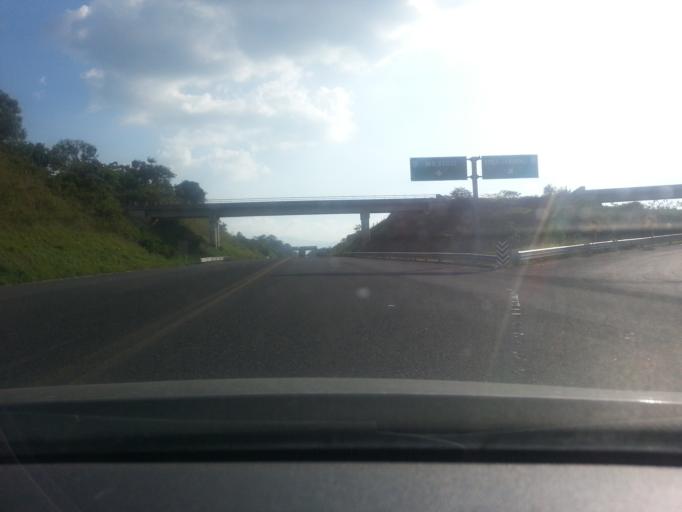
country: MX
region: Puebla
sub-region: Xicotepec
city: San Lorenzo
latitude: 20.4351
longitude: -97.9046
